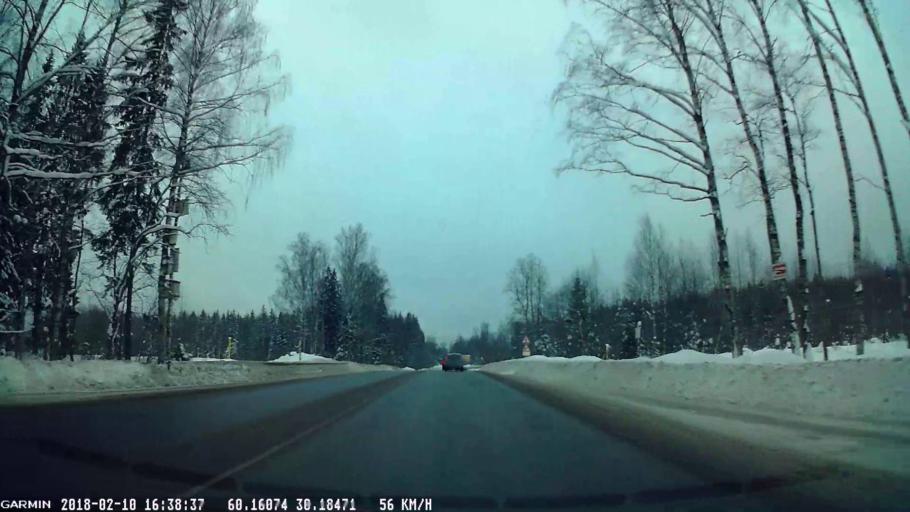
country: RU
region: Leningrad
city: Sertolovo
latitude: 60.1546
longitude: 30.1916
